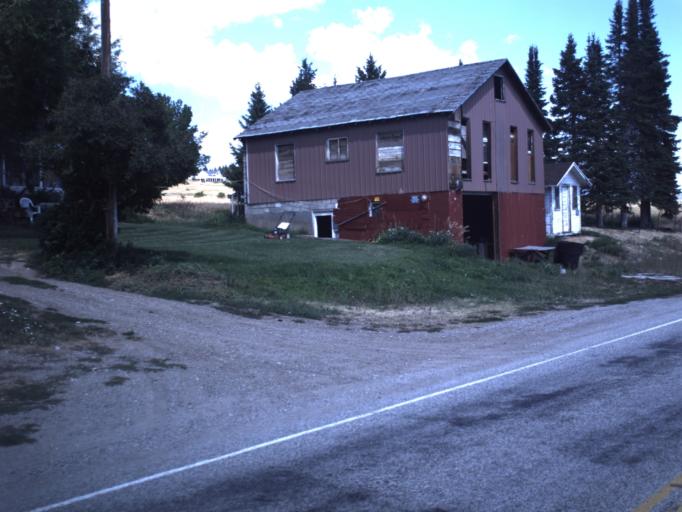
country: US
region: Idaho
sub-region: Bear Lake County
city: Paris
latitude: 41.9959
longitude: -111.4103
